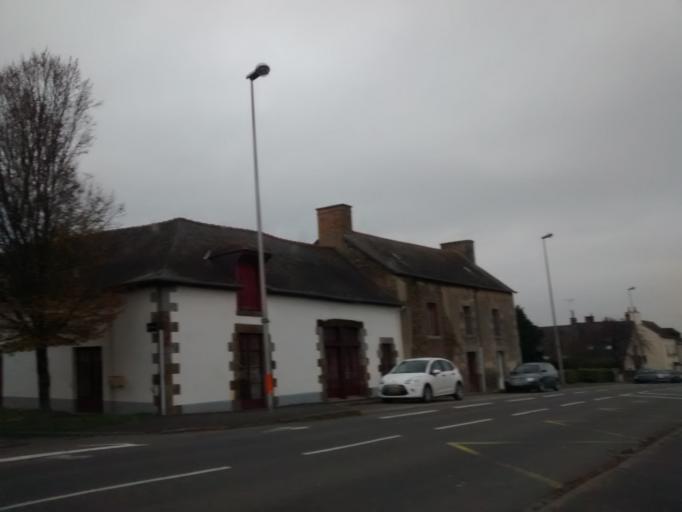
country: FR
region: Brittany
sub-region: Departement d'Ille-et-Vilaine
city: Noyal-sur-Vilaine
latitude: 48.1098
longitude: -1.5230
